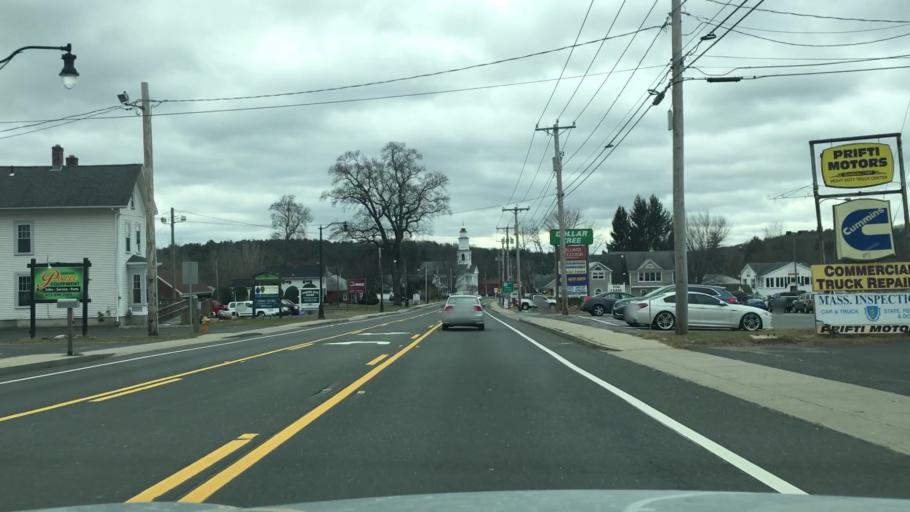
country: US
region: Massachusetts
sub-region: Hampden County
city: Southwick
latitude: 42.0580
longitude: -72.7678
